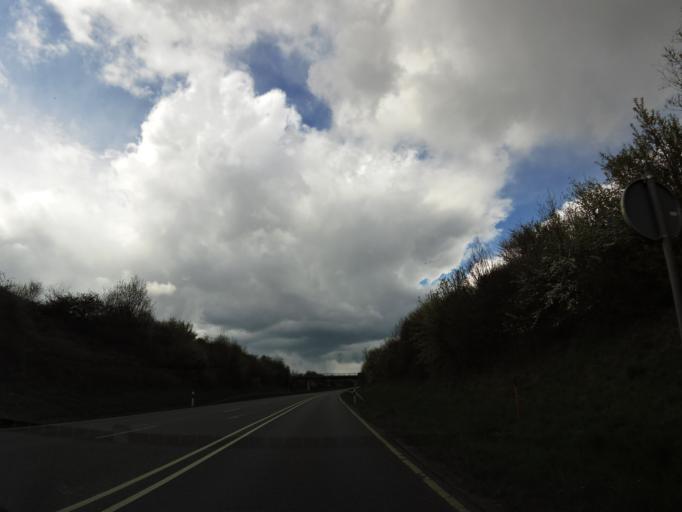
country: DE
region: Lower Saxony
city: Langelsheim
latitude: 51.9347
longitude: 10.3148
